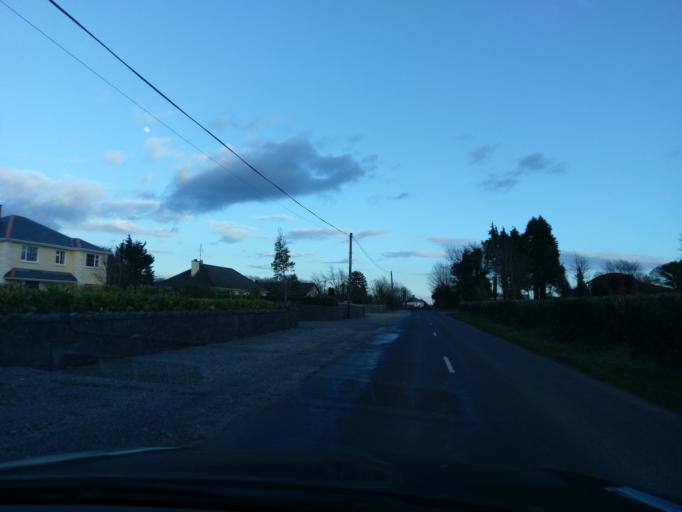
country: IE
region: Connaught
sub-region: County Galway
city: Athenry
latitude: 53.4292
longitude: -8.6971
